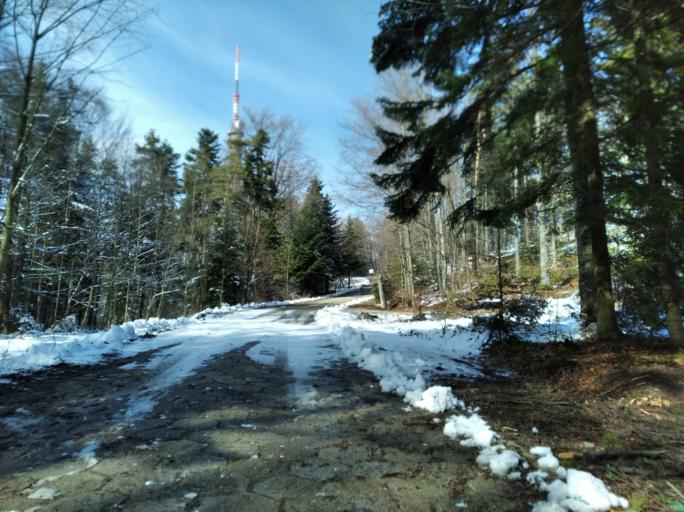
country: PL
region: Subcarpathian Voivodeship
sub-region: Powiat krosnienski
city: Korczyna
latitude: 49.7545
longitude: 21.8154
